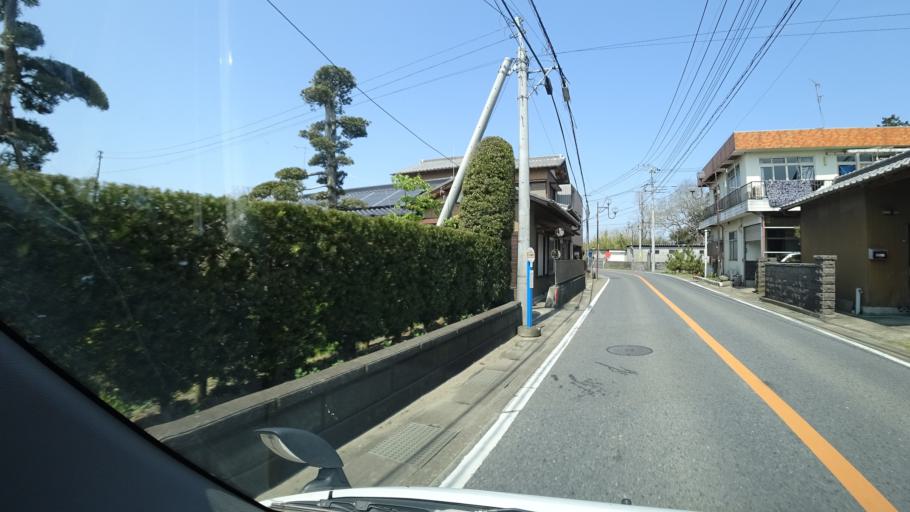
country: JP
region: Chiba
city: Yokaichiba
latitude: 35.6601
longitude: 140.4777
